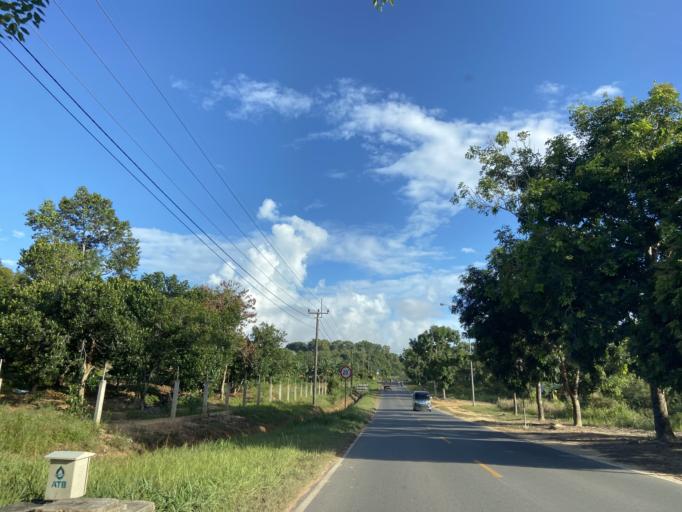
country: SG
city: Singapore
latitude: 1.0022
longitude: 104.0268
